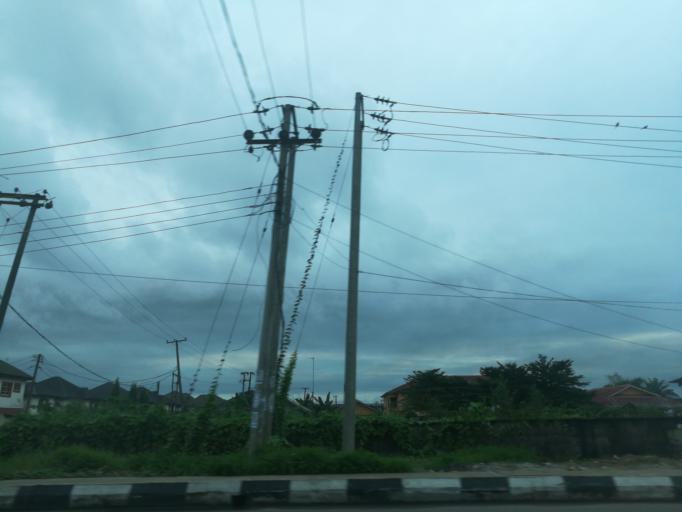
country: NG
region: Rivers
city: Port Harcourt
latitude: 4.8143
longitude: 6.9869
